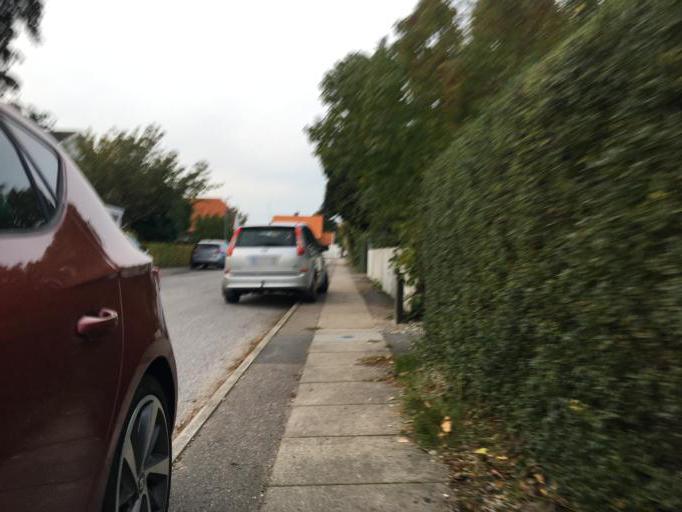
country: DK
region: Capital Region
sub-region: Tarnby Kommune
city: Tarnby
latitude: 55.6380
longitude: 12.6267
